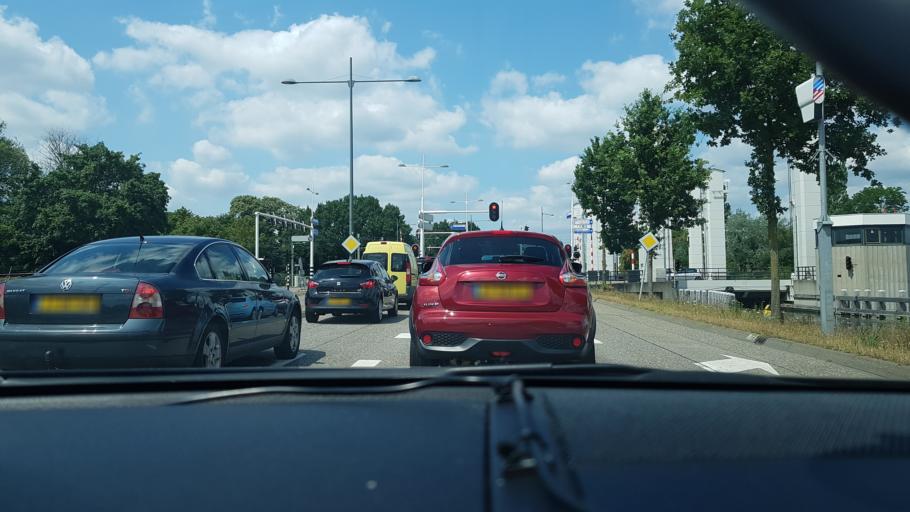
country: NL
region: North Brabant
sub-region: Gemeente Helmond
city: Helmond
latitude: 51.4726
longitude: 5.6544
